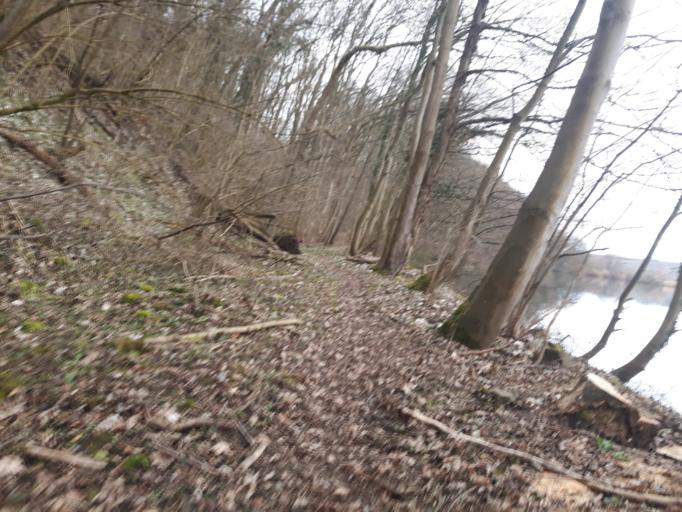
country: DE
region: Baden-Wuerttemberg
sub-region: Regierungsbezirk Stuttgart
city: Gemmrigheim
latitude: 49.0407
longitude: 9.1659
